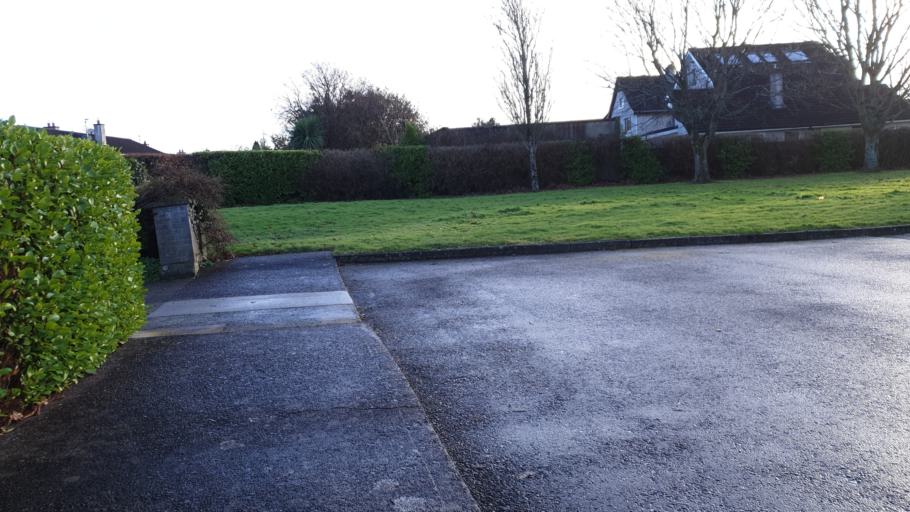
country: IE
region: Munster
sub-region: County Cork
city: Cork
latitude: 51.8934
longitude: -8.4250
